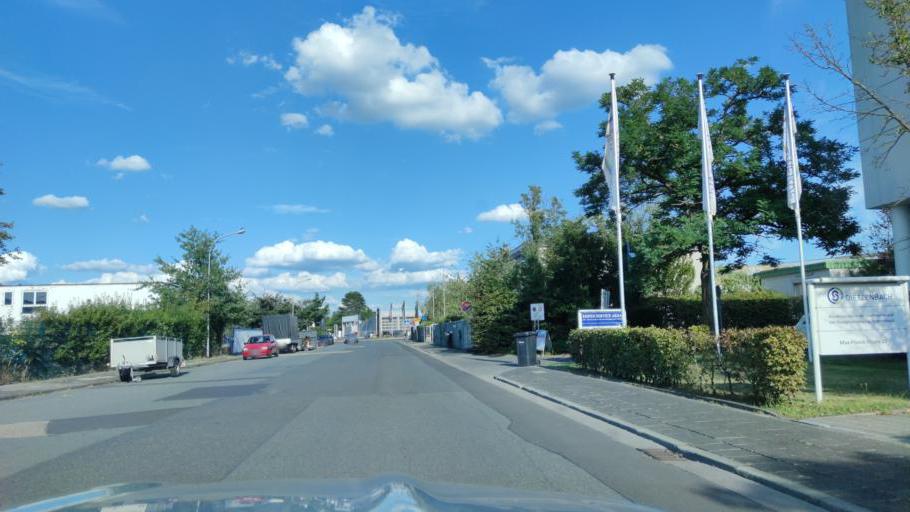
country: DE
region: Hesse
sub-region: Regierungsbezirk Darmstadt
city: Dietzenbach
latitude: 50.0046
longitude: 8.7913
